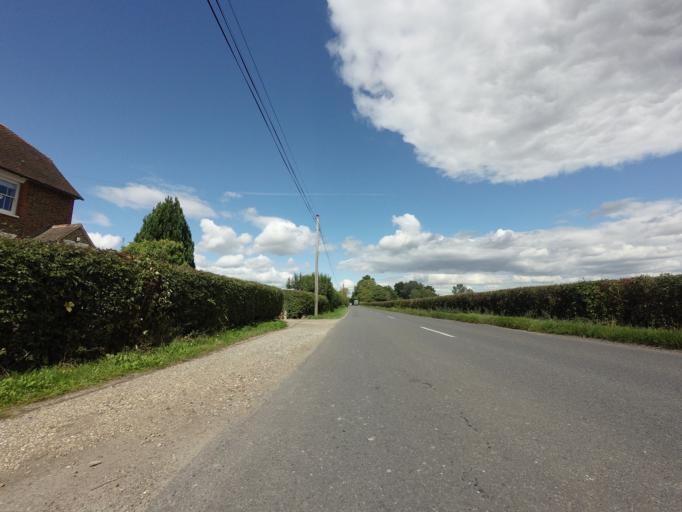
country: GB
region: England
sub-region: Kent
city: Marden
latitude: 51.1539
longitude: 0.4844
